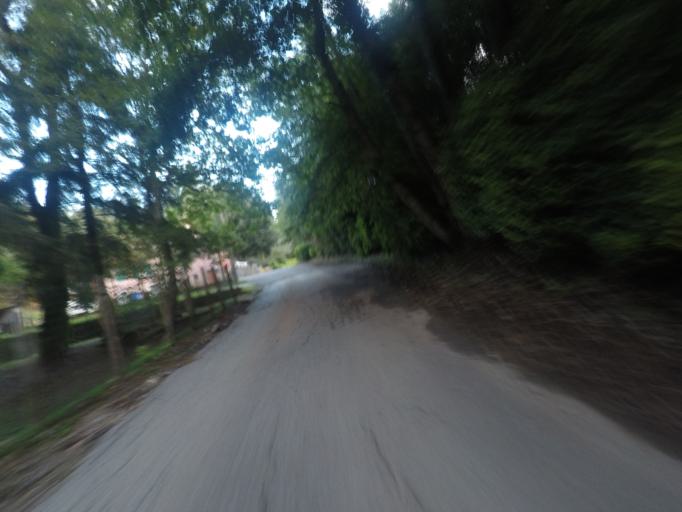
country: IT
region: Tuscany
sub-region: Provincia di Lucca
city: Pescaglia
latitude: 43.9359
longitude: 10.3820
